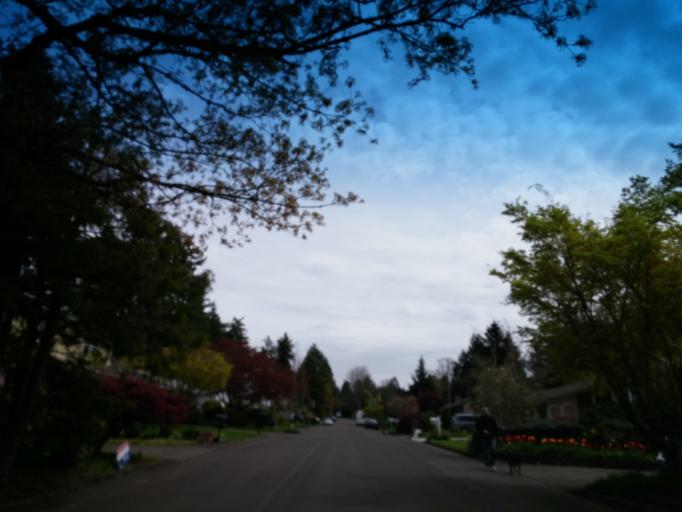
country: US
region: Oregon
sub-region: Washington County
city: Cedar Mill
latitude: 45.5332
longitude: -122.8144
